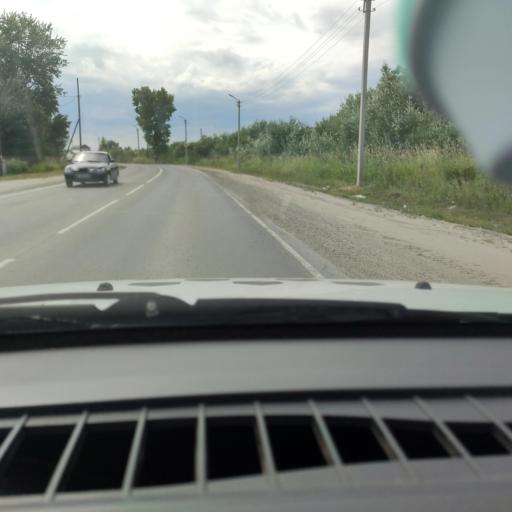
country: RU
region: Perm
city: Solikamsk
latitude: 59.6759
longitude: 56.7717
